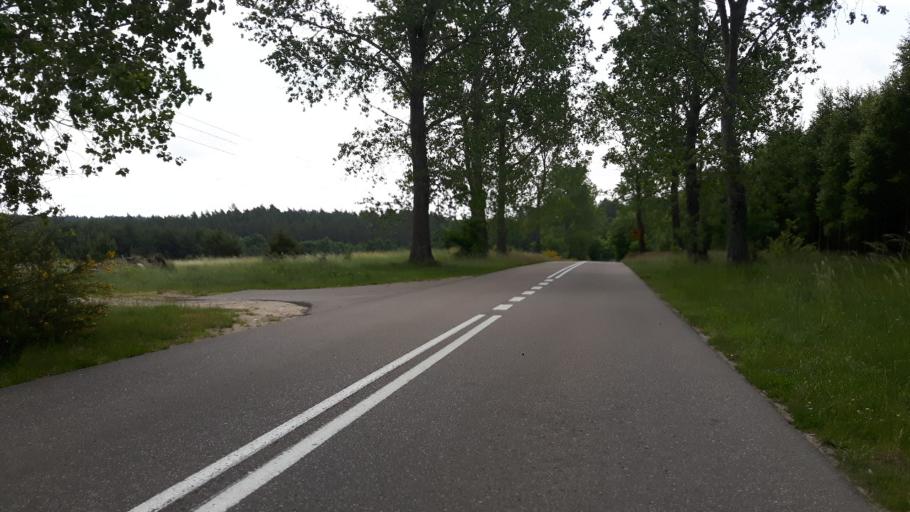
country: PL
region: Pomeranian Voivodeship
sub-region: Powiat leborski
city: Leba
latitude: 54.7534
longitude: 17.7101
